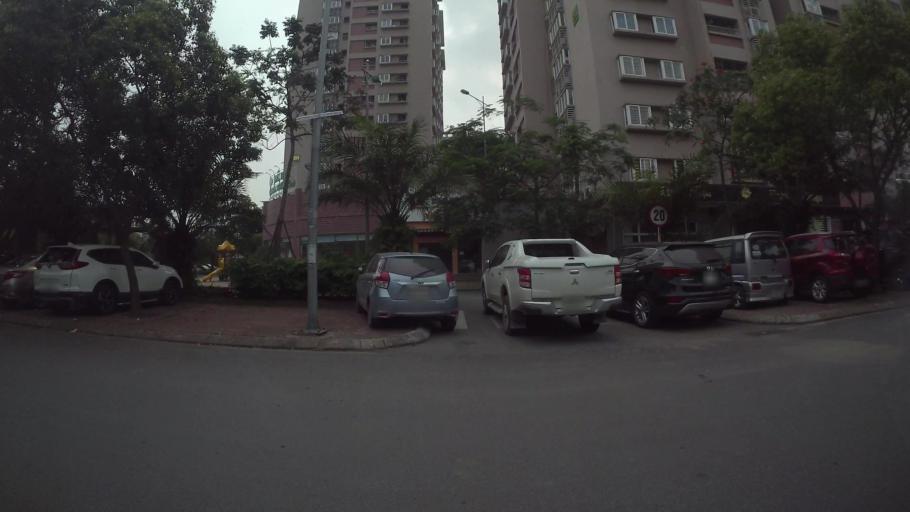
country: VN
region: Ha Noi
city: Trau Quy
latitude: 21.0583
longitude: 105.9074
